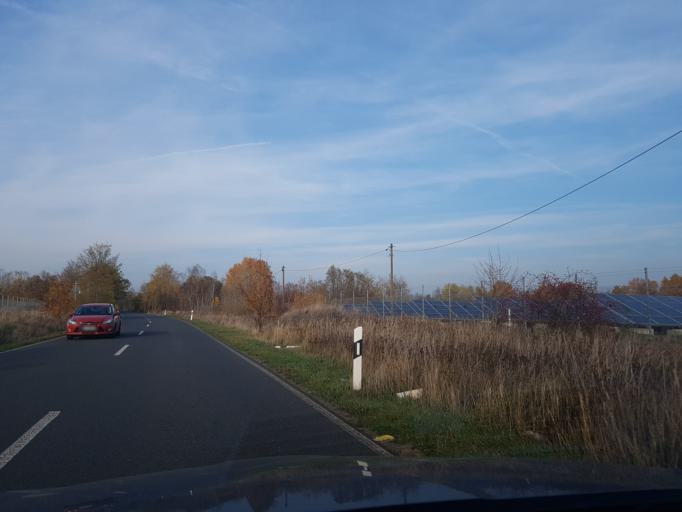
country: DE
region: Brandenburg
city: Falkenberg
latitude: 51.5511
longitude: 13.2282
